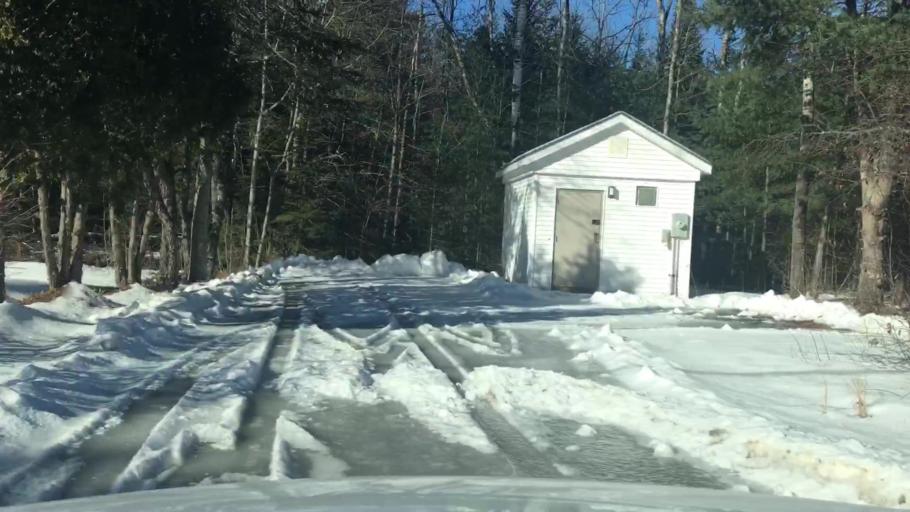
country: US
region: Maine
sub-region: Androscoggin County
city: Lisbon Falls
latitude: 43.9861
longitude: -70.0987
